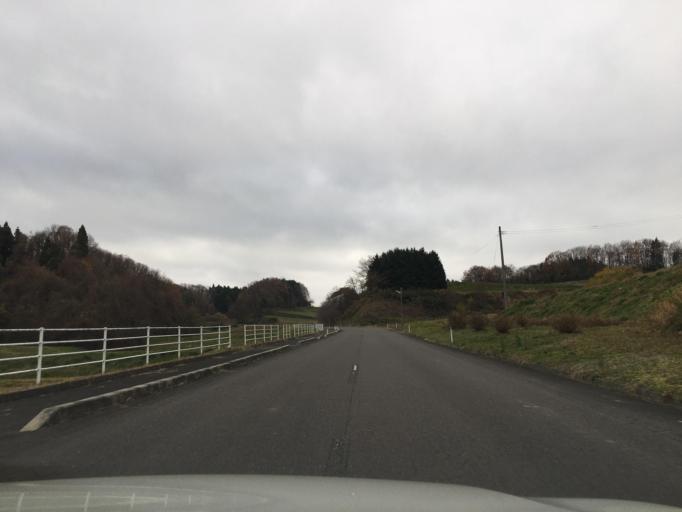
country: JP
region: Fukushima
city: Funehikimachi-funehiki
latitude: 37.4708
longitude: 140.5471
